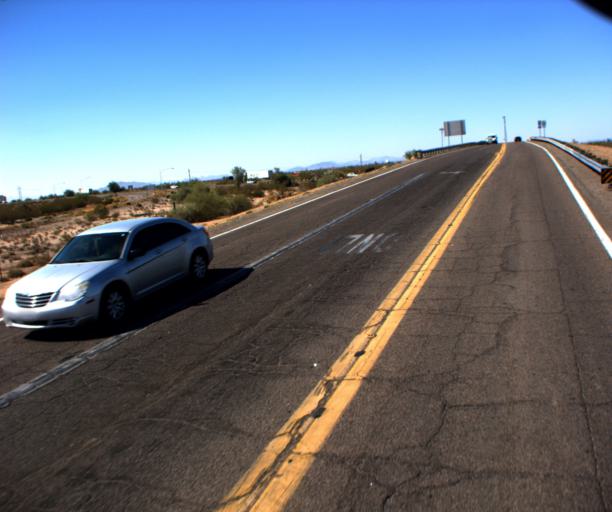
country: US
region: Arizona
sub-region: Pinal County
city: Sacaton
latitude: 33.0045
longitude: -111.7522
